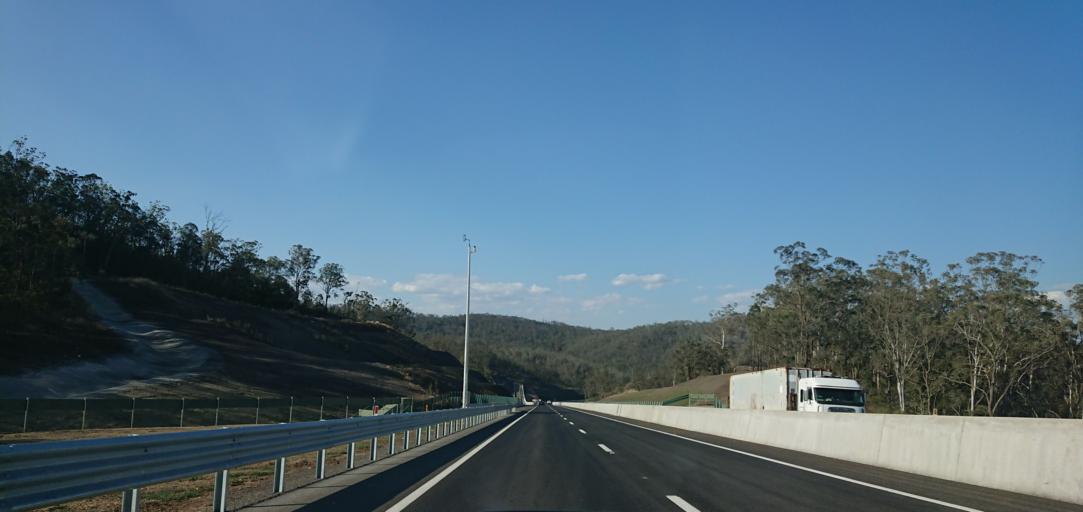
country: AU
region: Queensland
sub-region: Toowoomba
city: Wilsonton Heights
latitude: -27.5058
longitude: 151.9713
